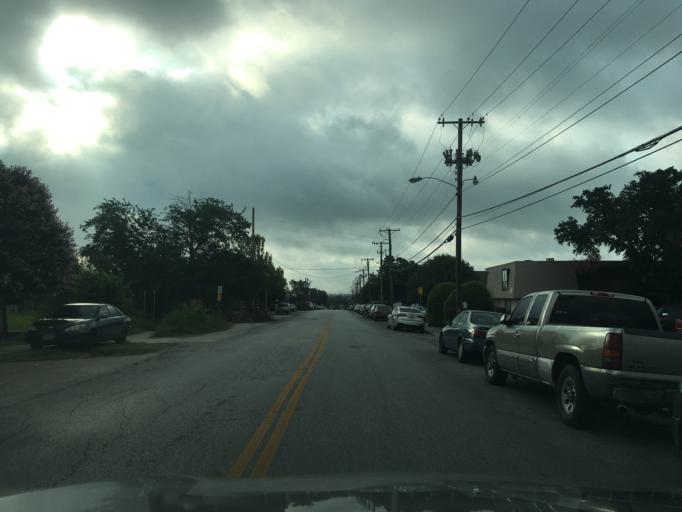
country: US
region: Texas
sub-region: Dallas County
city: University Park
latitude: 32.8667
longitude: -96.7544
